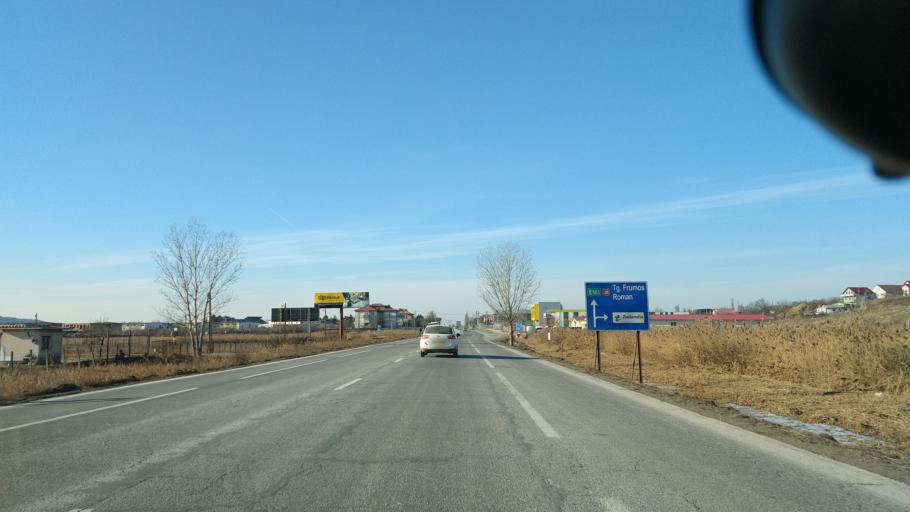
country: RO
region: Iasi
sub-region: Comuna Letcani
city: Letcani
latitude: 47.1842
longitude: 27.4576
